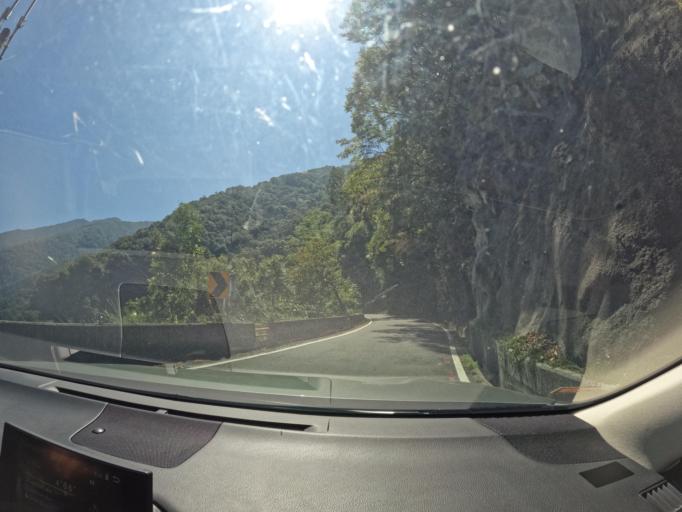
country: TW
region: Taiwan
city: Yujing
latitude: 23.2902
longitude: 120.8538
